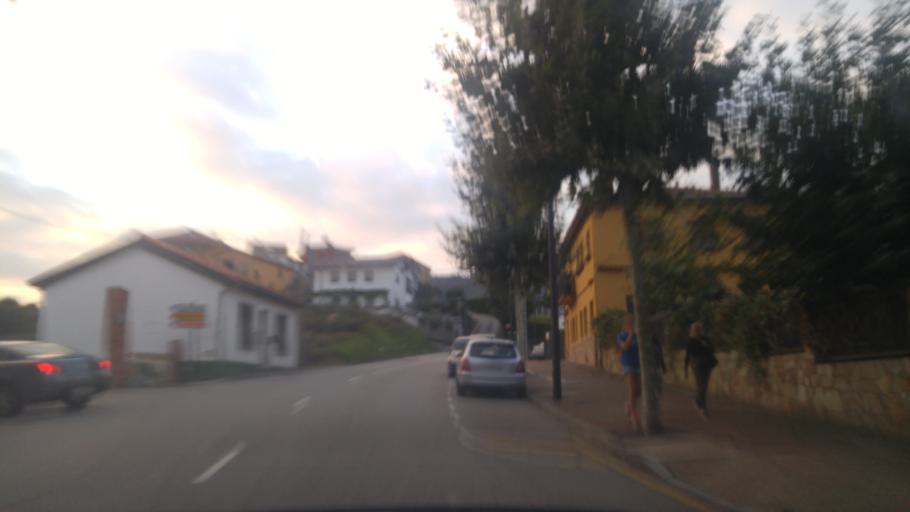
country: ES
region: Asturias
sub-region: Province of Asturias
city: Oviedo
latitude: 43.3729
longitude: -5.8617
